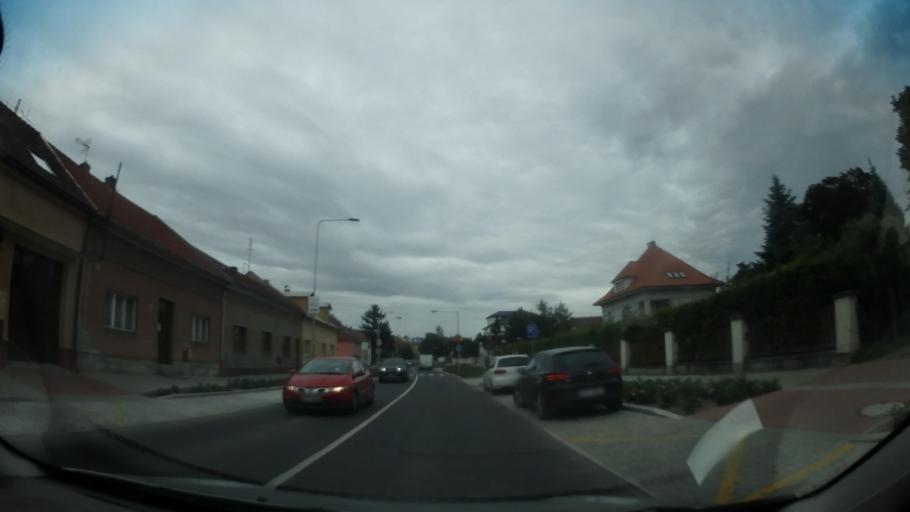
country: CZ
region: Central Bohemia
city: Lysa nad Labem
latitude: 50.2046
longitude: 14.8433
